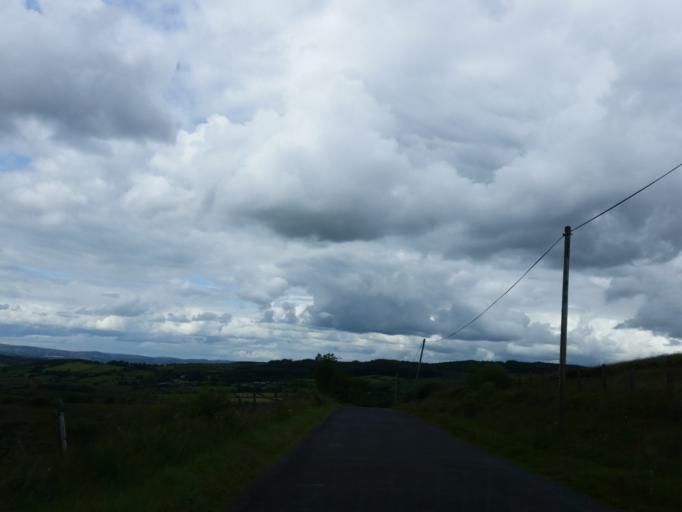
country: GB
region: Northern Ireland
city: Fivemiletown
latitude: 54.2835
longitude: -7.2760
